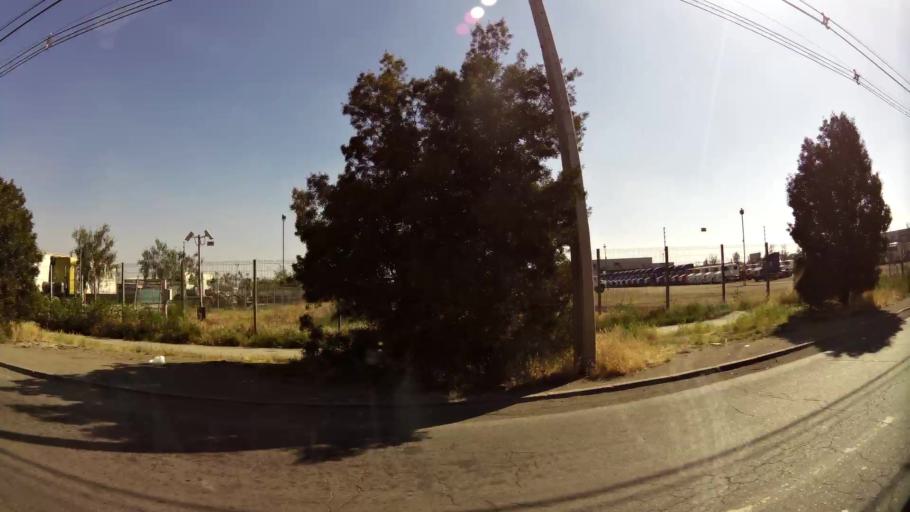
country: CL
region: Santiago Metropolitan
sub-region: Provincia de Chacabuco
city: Chicureo Abajo
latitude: -33.3304
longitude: -70.7121
